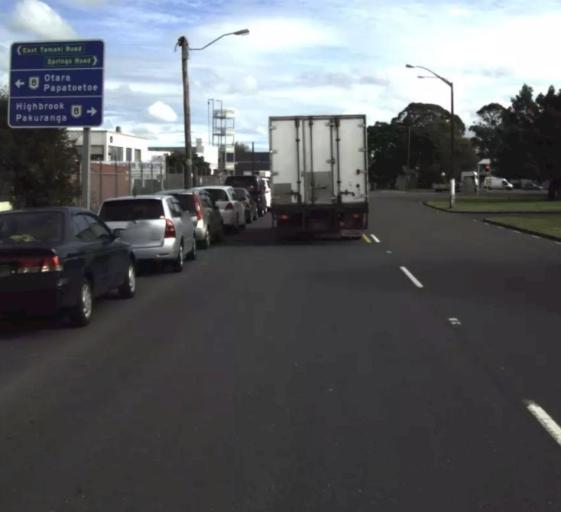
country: NZ
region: Auckland
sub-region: Auckland
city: Manukau City
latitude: -36.9539
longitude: 174.8927
